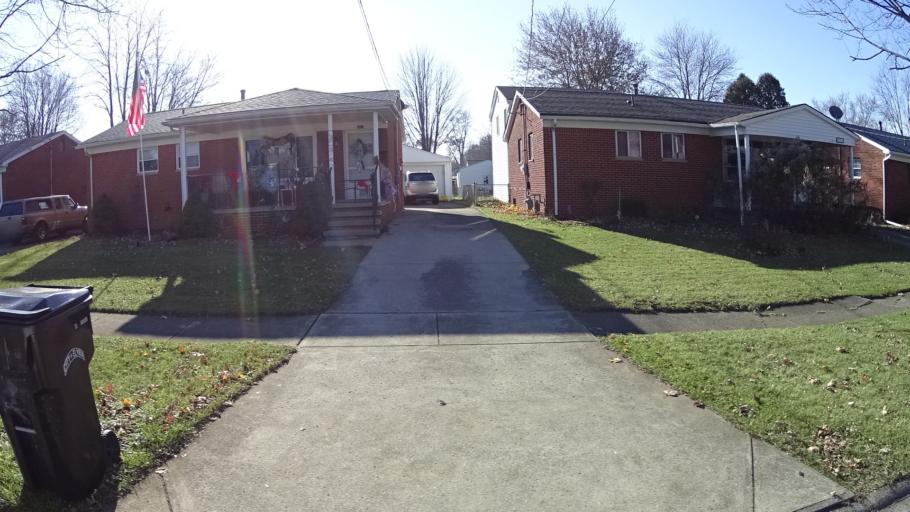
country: US
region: Ohio
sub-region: Lorain County
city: Sheffield
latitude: 41.3966
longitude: -82.0739
